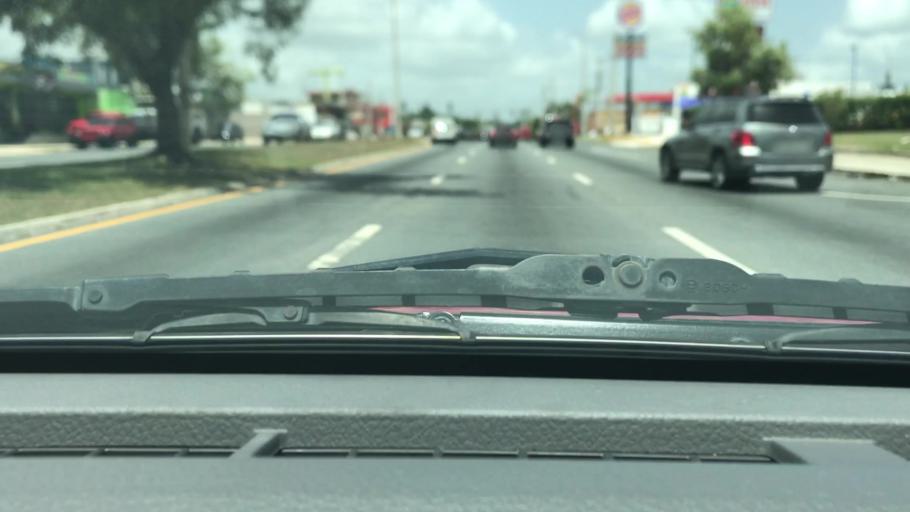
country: PR
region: Bayamon
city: Bayamon
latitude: 18.3654
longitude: -66.1741
